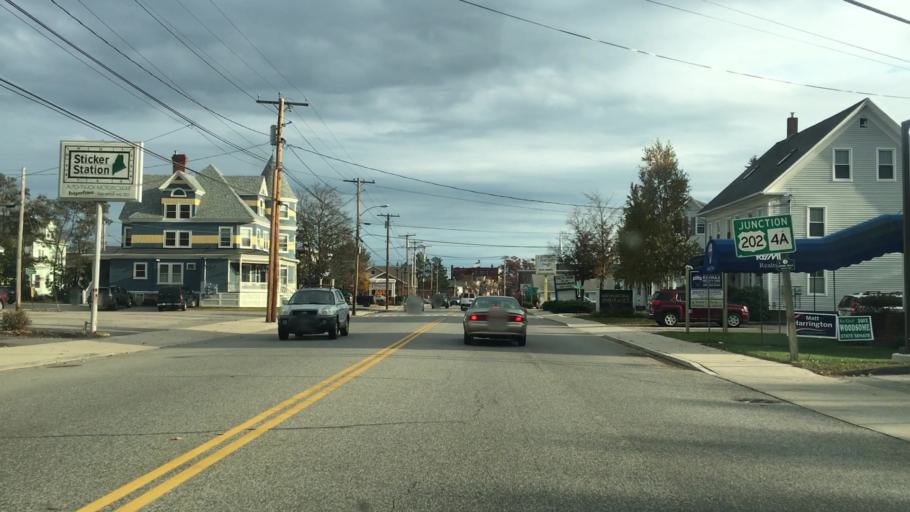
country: US
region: Maine
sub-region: York County
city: Sanford (historical)
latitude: 43.4422
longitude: -70.7797
